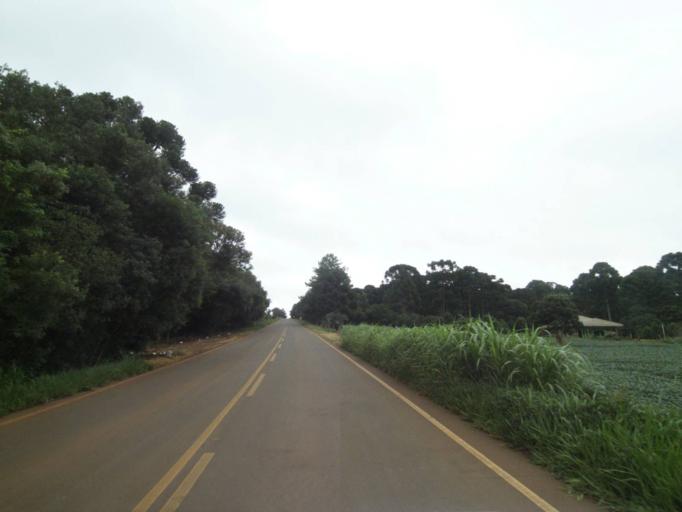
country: BR
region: Parana
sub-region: Pitanga
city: Pitanga
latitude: -24.9329
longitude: -51.8826
